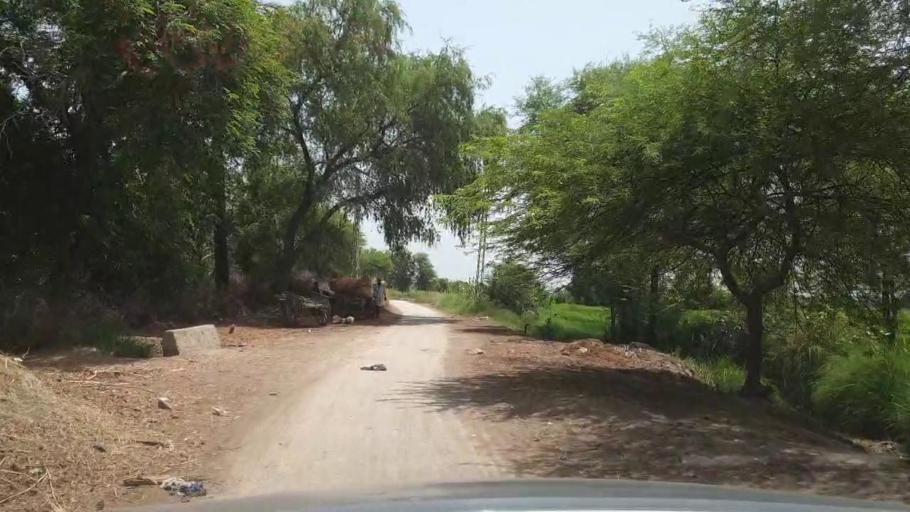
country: PK
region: Sindh
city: Ratodero
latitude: 27.8027
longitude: 68.3405
